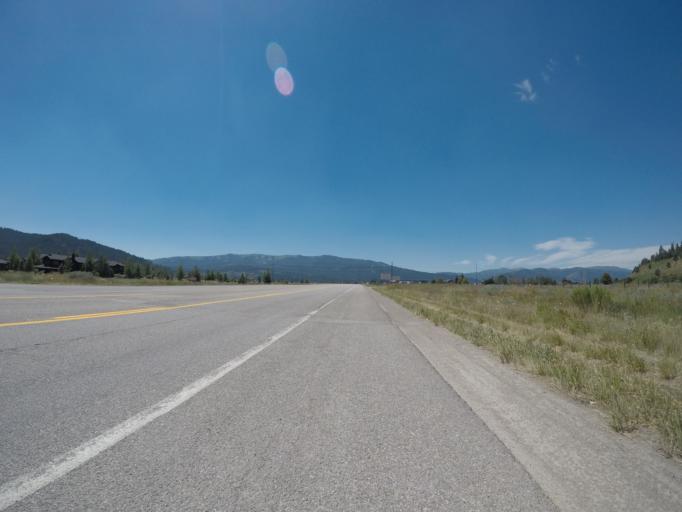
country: US
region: Wyoming
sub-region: Teton County
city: Hoback
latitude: 43.1736
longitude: -111.0121
